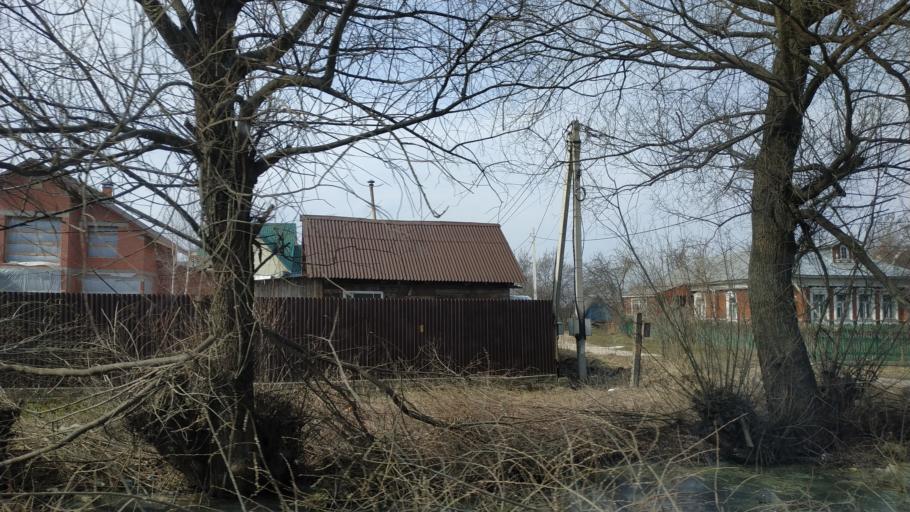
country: RU
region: Moskovskaya
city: Bronnitsy
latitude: 55.3872
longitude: 38.3477
